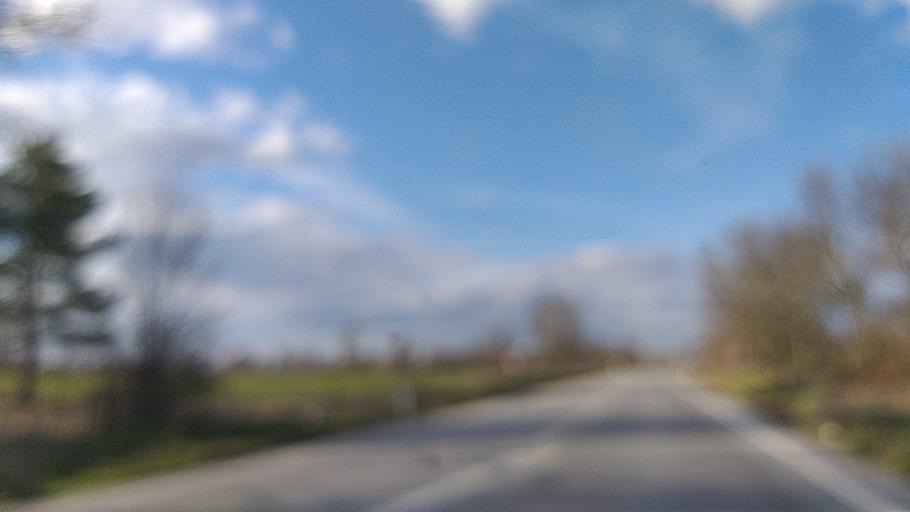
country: ES
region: Castille and Leon
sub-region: Provincia de Salamanca
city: Fuentes de Onoro
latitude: 40.6377
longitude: -6.8558
